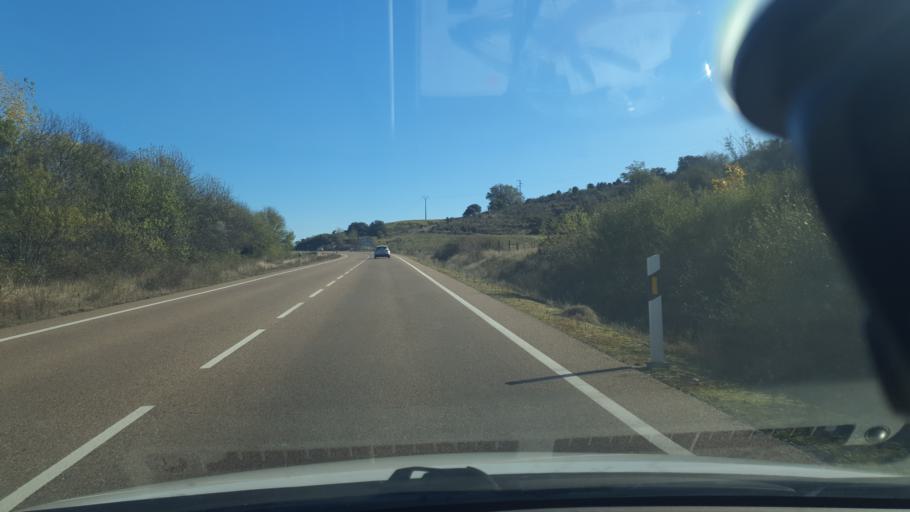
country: ES
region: Castille and Leon
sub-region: Provincia de Avila
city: Poyales del Hoyo
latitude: 40.1578
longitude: -5.1752
